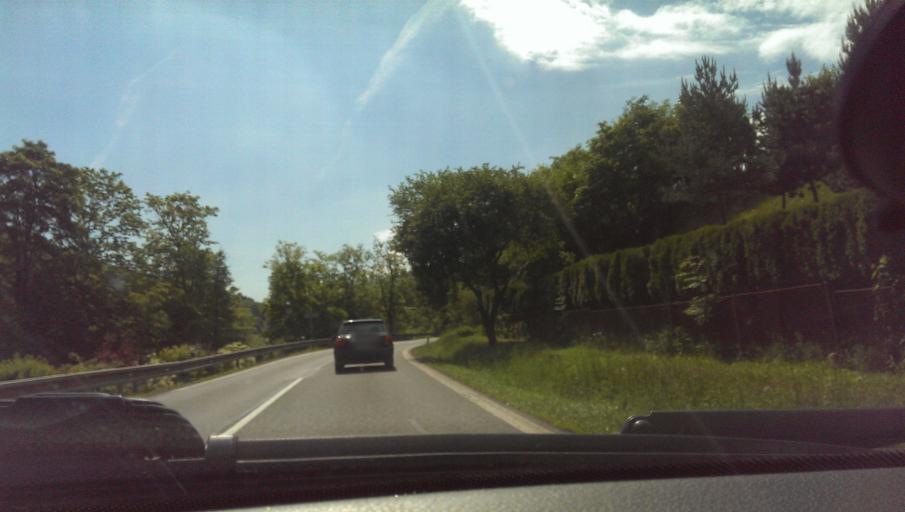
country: CZ
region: Zlin
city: Valasska Polanka
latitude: 49.2513
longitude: 18.0003
